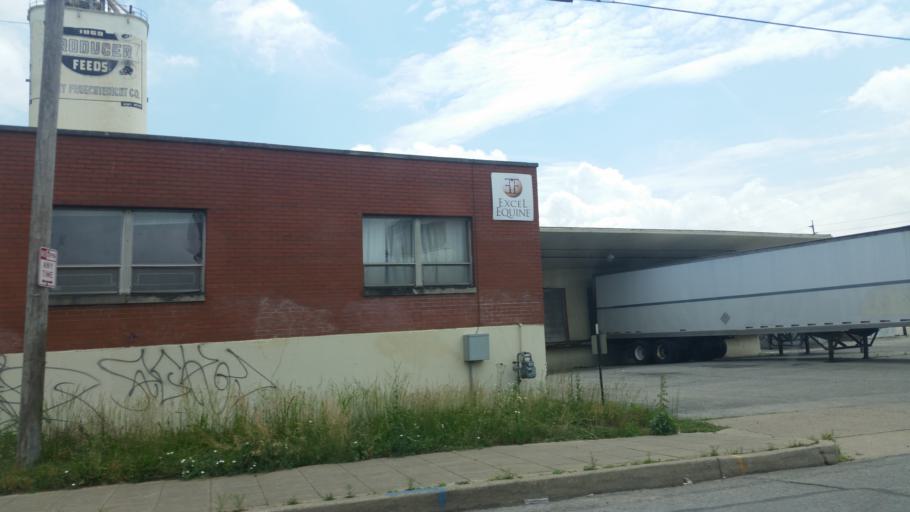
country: US
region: Indiana
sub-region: Clark County
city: Jeffersonville
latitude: 38.2574
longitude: -85.7394
